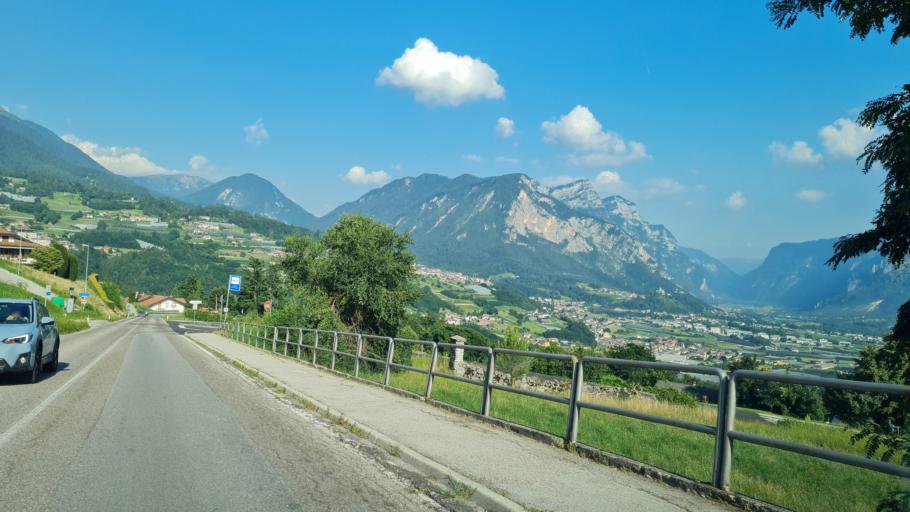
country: IT
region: Trentino-Alto Adige
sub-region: Provincia di Trento
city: Telve
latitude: 46.0726
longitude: 11.4837
